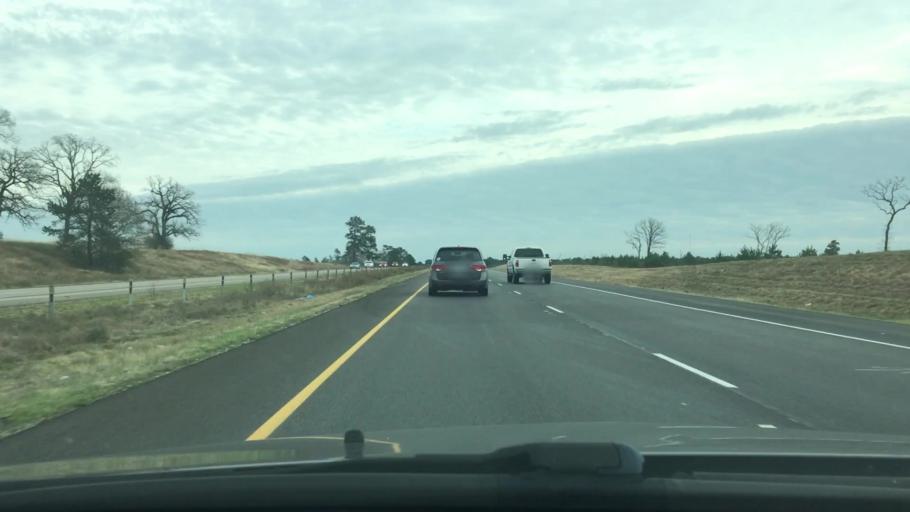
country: US
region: Texas
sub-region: Madison County
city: Madisonville
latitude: 30.8458
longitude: -95.7309
